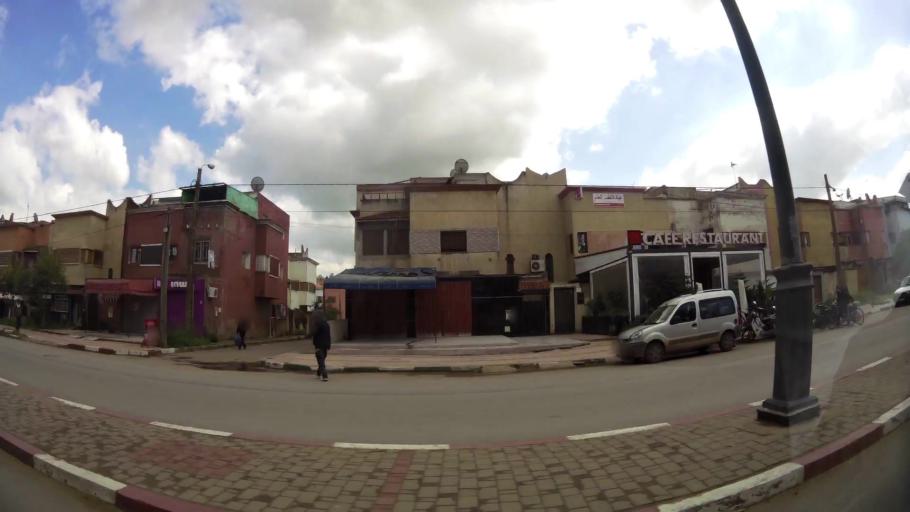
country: MA
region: Grand Casablanca
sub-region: Mediouna
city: Mediouna
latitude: 33.3725
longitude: -7.5324
